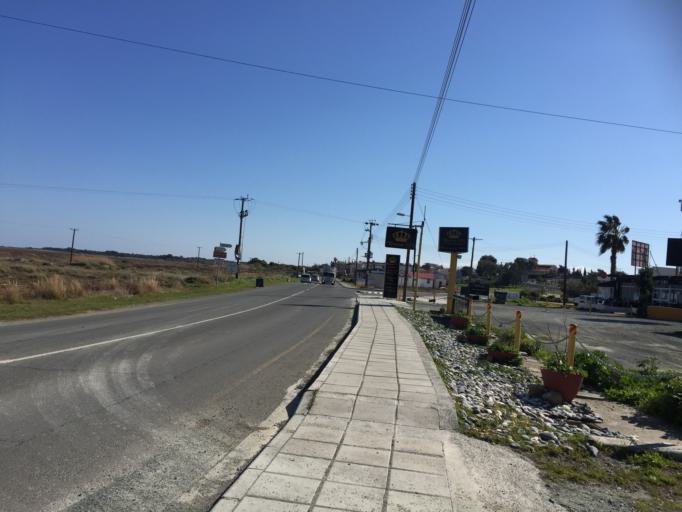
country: CY
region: Larnaka
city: Kolossi
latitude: 34.6049
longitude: 32.9514
